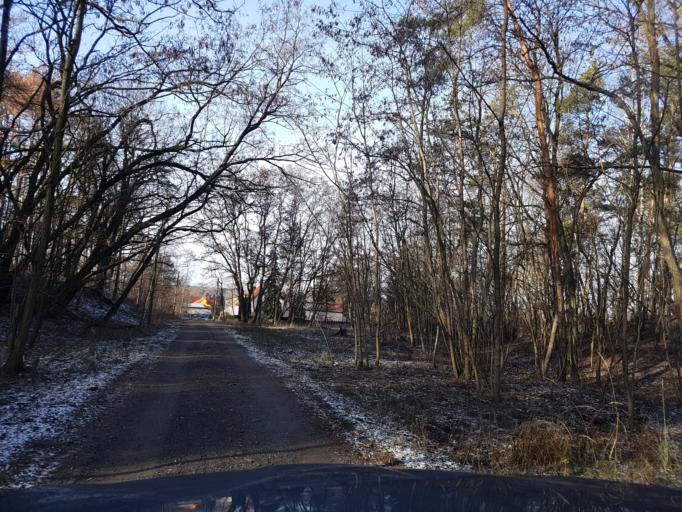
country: DE
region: Brandenburg
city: Schonborn
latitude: 51.5412
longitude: 13.4803
